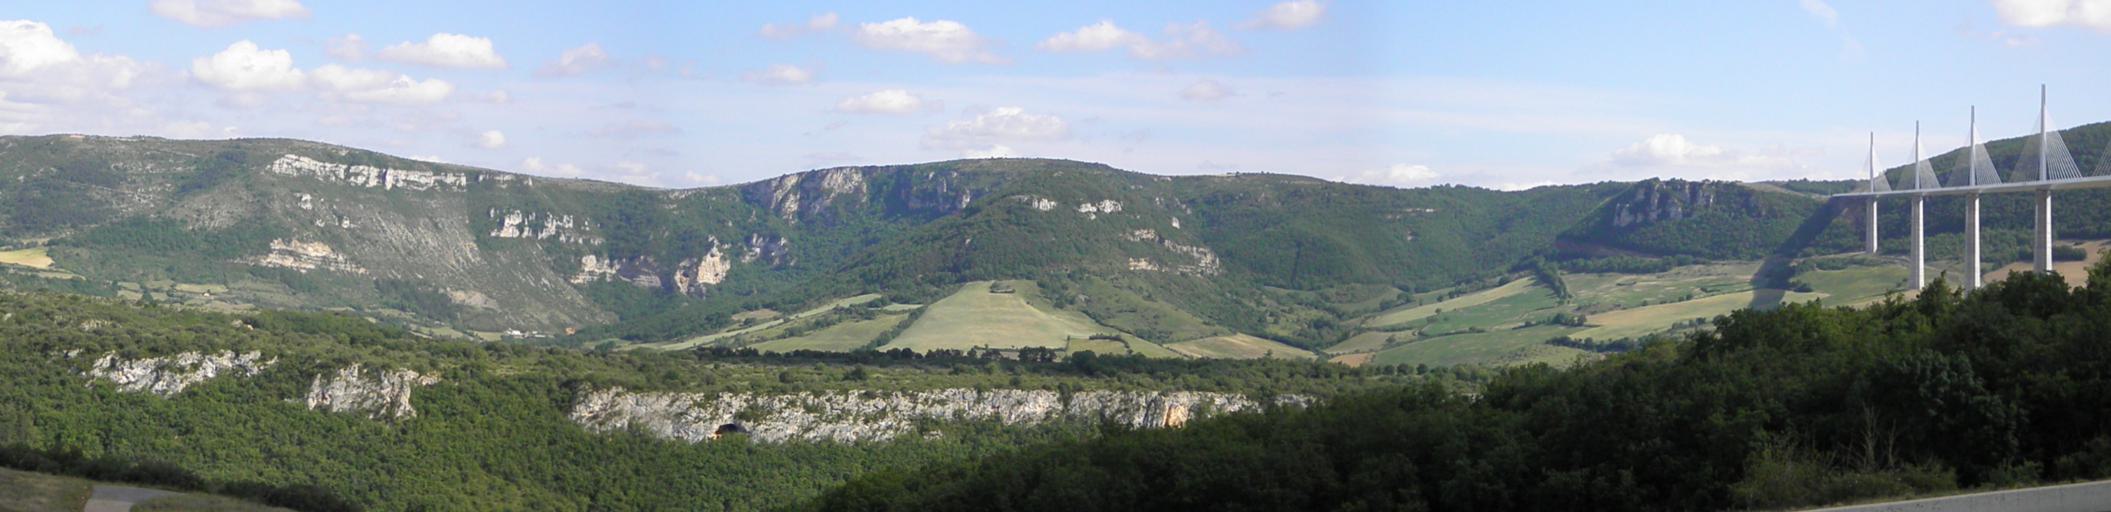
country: FR
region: Midi-Pyrenees
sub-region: Departement de l'Aveyron
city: Creissels
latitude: 44.0936
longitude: 3.0235
